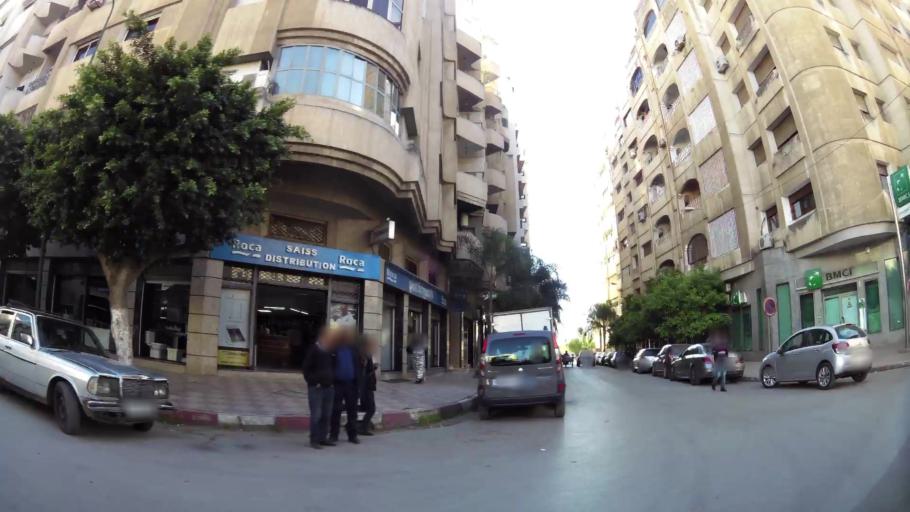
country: MA
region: Meknes-Tafilalet
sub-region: Meknes
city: Meknes
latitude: 33.8951
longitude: -5.5428
